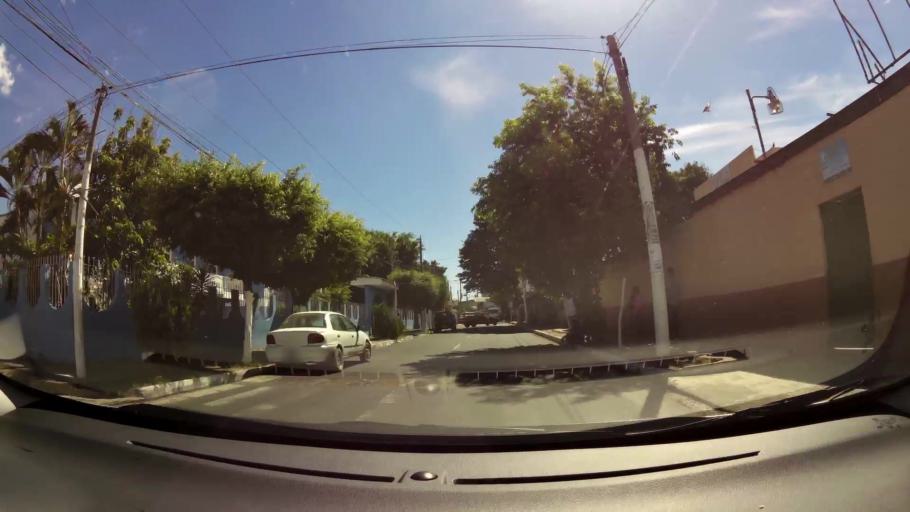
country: SV
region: San Salvador
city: Apopa
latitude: 13.8048
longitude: -89.1797
